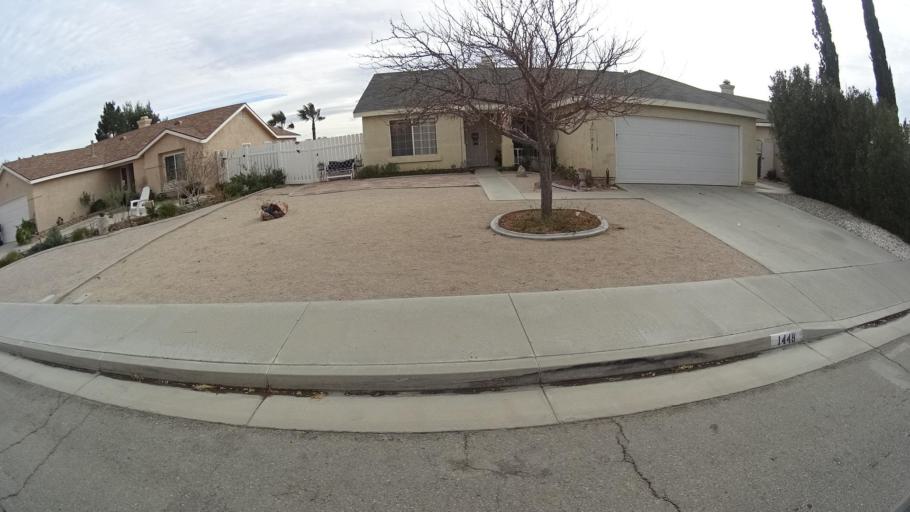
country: US
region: California
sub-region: Kern County
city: Rosamond
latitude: 34.8785
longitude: -118.1577
